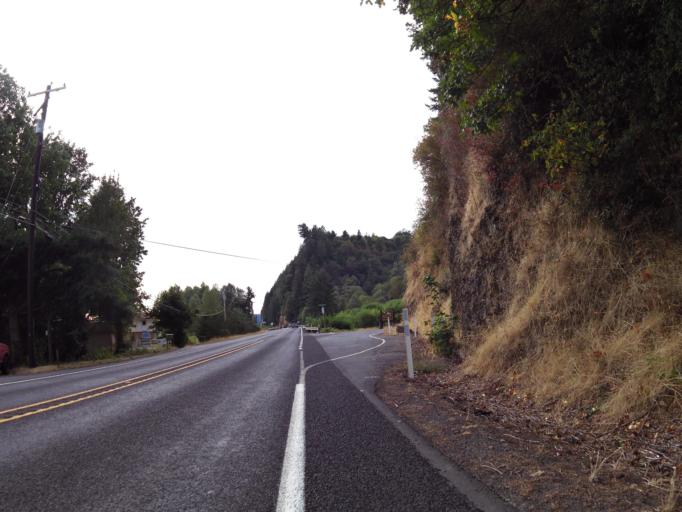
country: US
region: Washington
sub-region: Cowlitz County
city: West Longview
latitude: 46.1901
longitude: -123.1205
